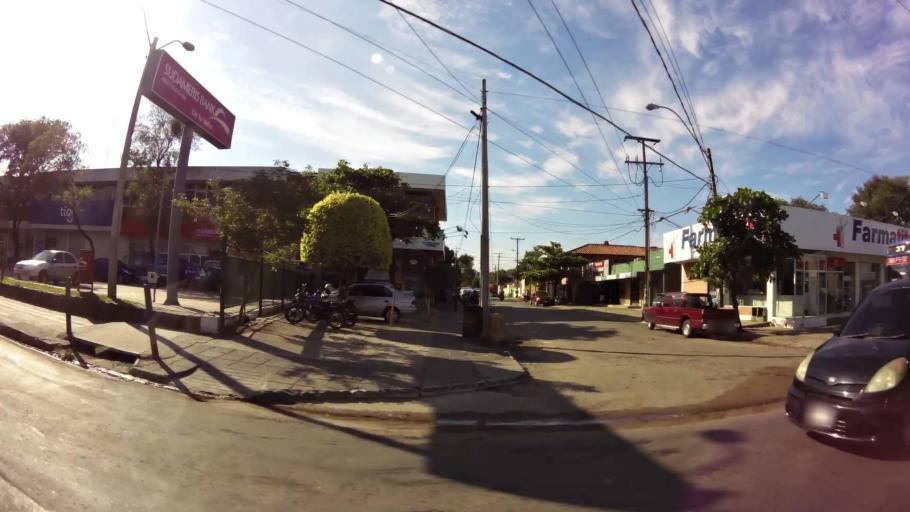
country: PY
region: Asuncion
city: Asuncion
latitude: -25.2586
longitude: -57.5870
